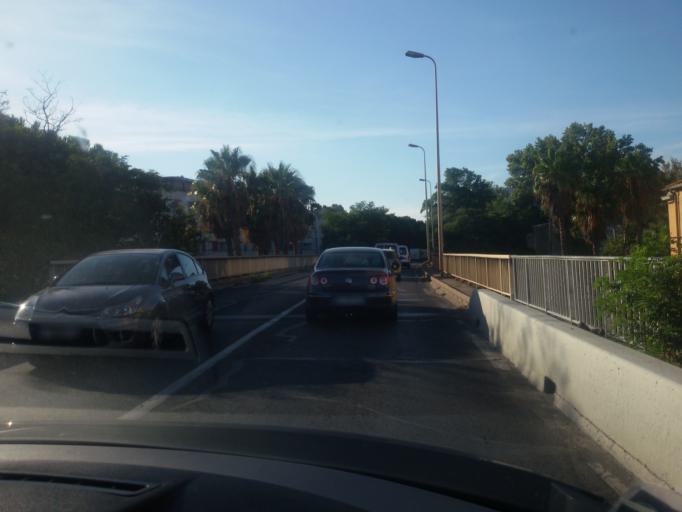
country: FR
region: Languedoc-Roussillon
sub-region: Departement de l'Herault
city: Montpellier
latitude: 43.6009
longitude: 3.8686
